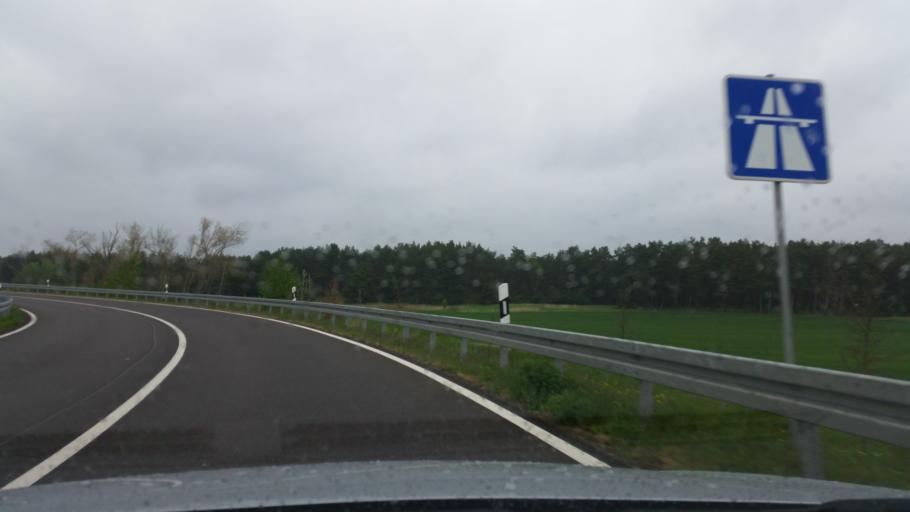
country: DE
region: Saxony-Anhalt
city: Colbitz
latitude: 52.3324
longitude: 11.6179
